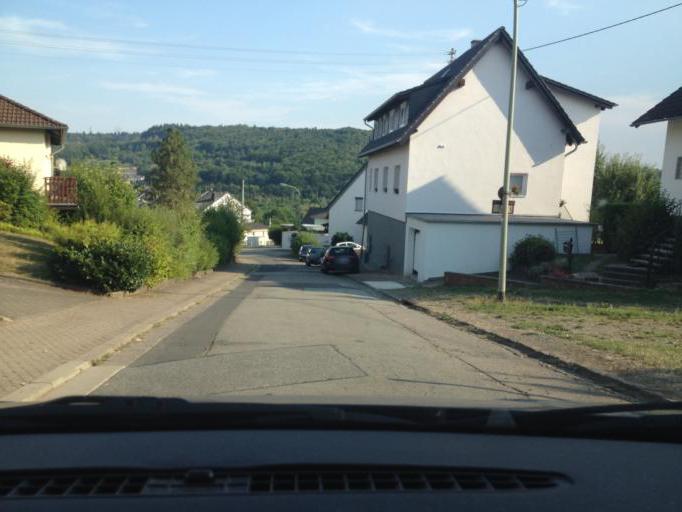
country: DE
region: Saarland
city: Sankt Wendel
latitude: 49.4545
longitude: 7.1456
